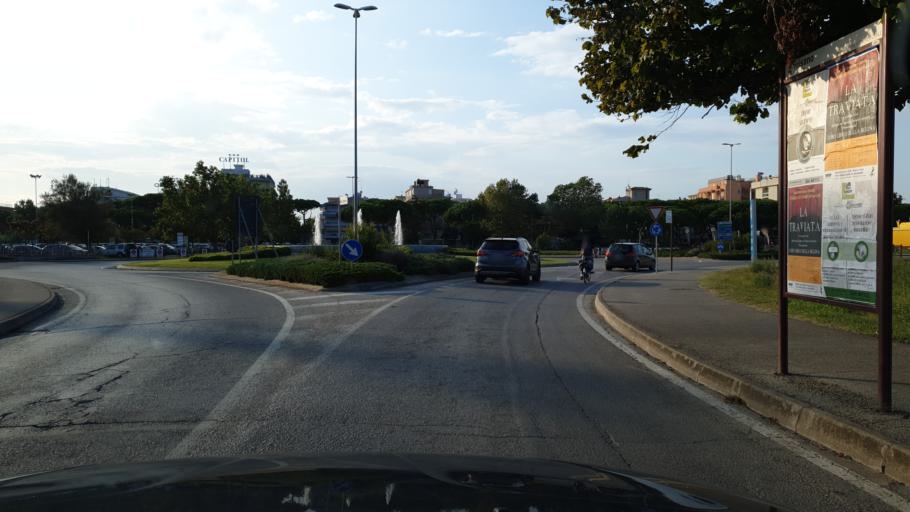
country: IT
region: Emilia-Romagna
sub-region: Provincia di Rimini
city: Misano Adriatico
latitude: 43.9822
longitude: 12.6909
